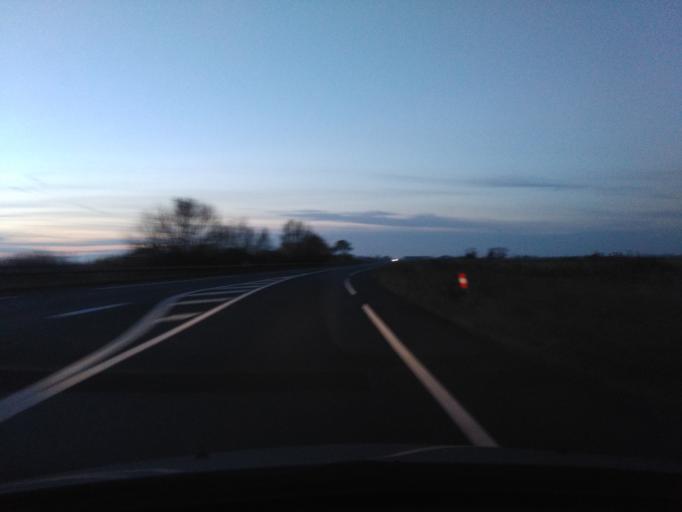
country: FR
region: Pays de la Loire
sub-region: Departement de la Vendee
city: Champagne-les-Marais
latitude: 46.4159
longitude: -1.1000
